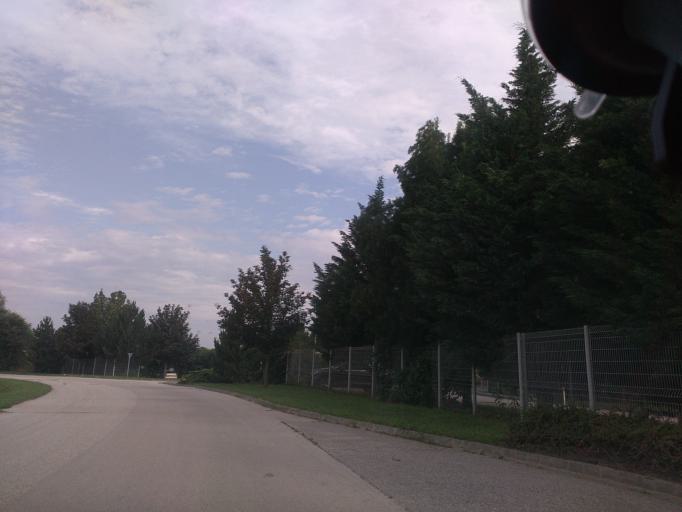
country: HU
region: Komarom-Esztergom
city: Piliscsev
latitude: 47.6754
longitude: 18.7886
